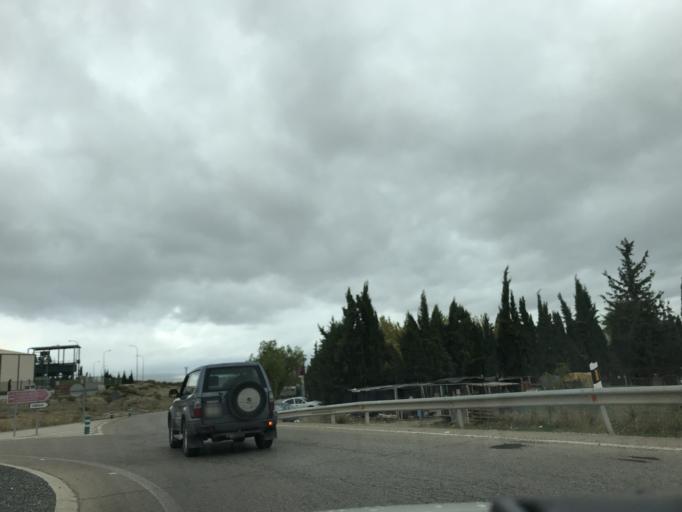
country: ES
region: Andalusia
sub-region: Provincia de Jaen
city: Peal de Becerro
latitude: 37.9186
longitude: -3.1317
